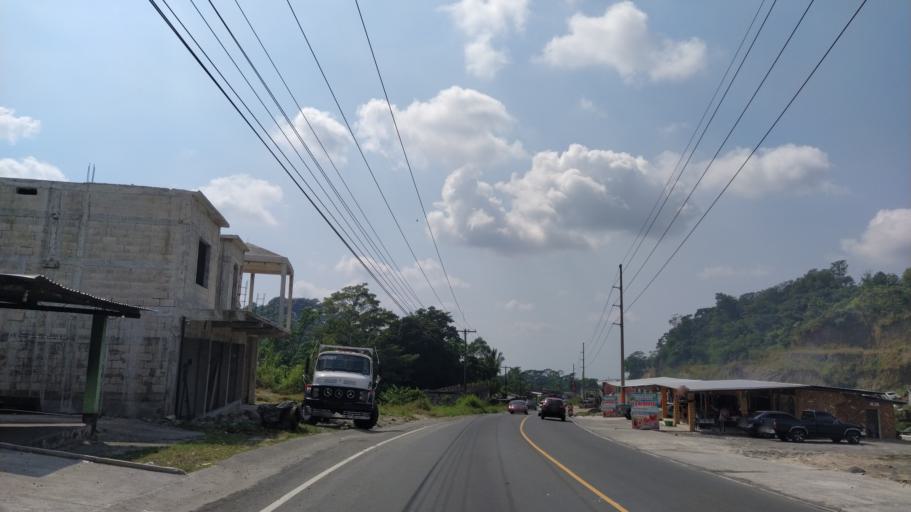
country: GT
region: Quetzaltenango
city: El Palmar
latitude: 14.6449
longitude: -91.5713
